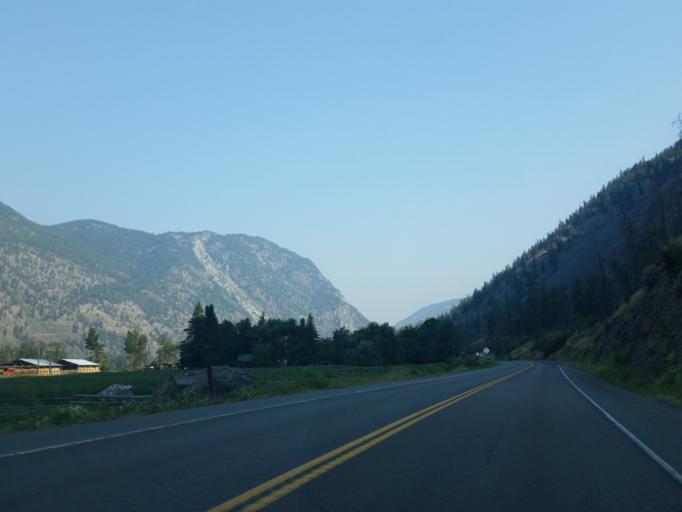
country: CA
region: British Columbia
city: Oliver
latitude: 49.2680
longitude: -120.0190
